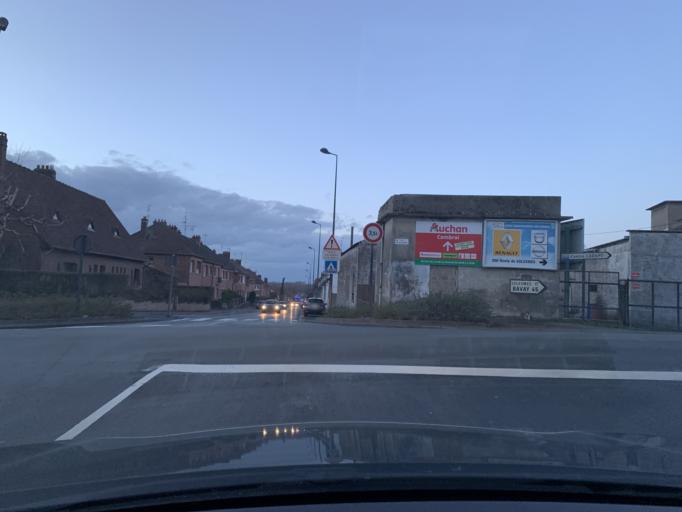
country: FR
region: Nord-Pas-de-Calais
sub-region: Departement du Nord
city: Cambrai
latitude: 50.1787
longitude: 3.2537
